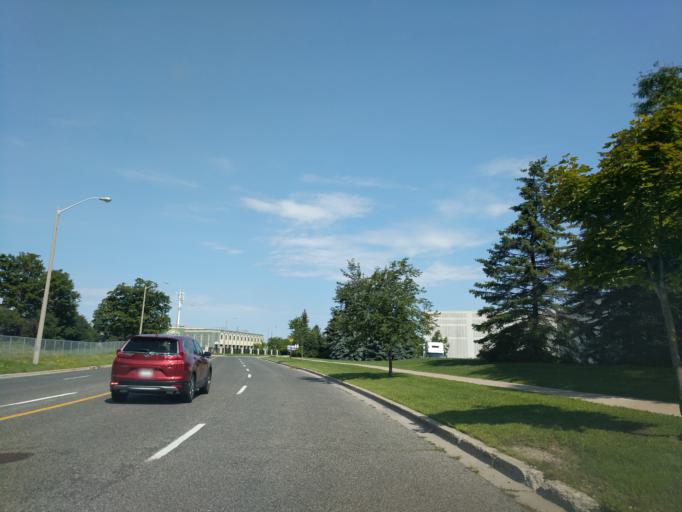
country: CA
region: Ontario
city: Scarborough
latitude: 43.8172
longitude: -79.2279
